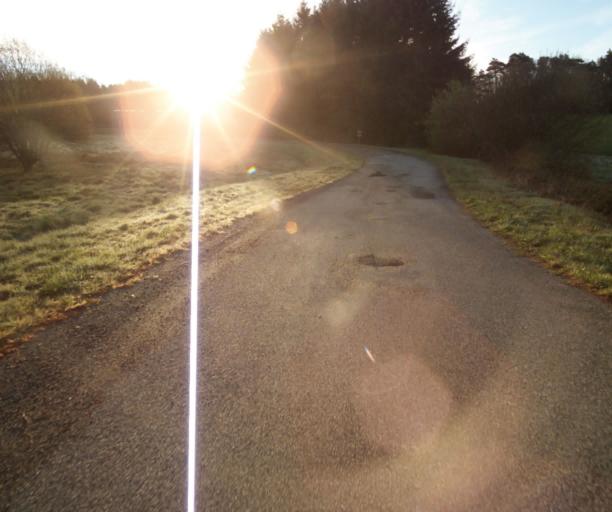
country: FR
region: Limousin
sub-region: Departement de la Correze
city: Correze
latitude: 45.3172
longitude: 1.8468
